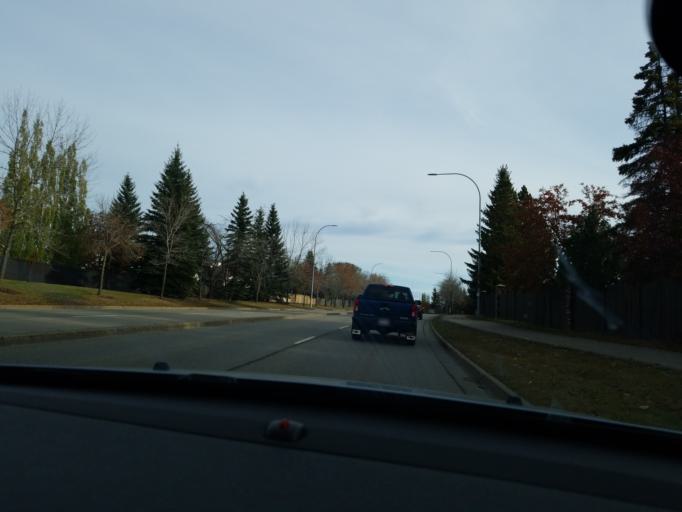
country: CA
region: Alberta
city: Sherwood Park
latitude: 53.5264
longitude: -113.2764
